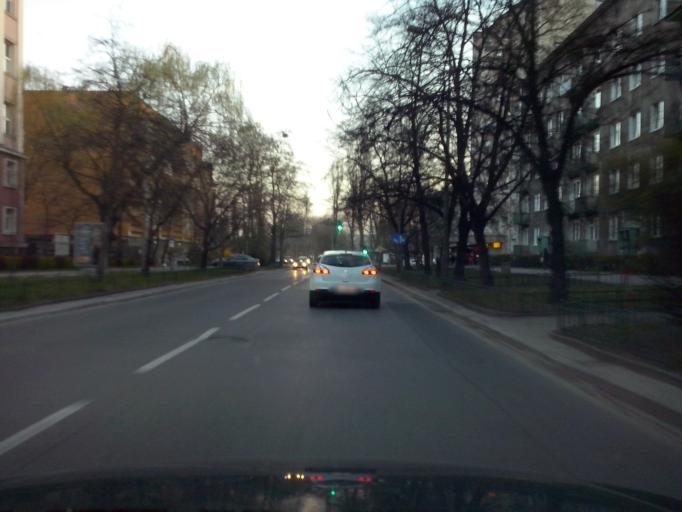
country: PL
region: Lesser Poland Voivodeship
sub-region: Krakow
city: Krakow
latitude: 50.0724
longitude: 19.9150
